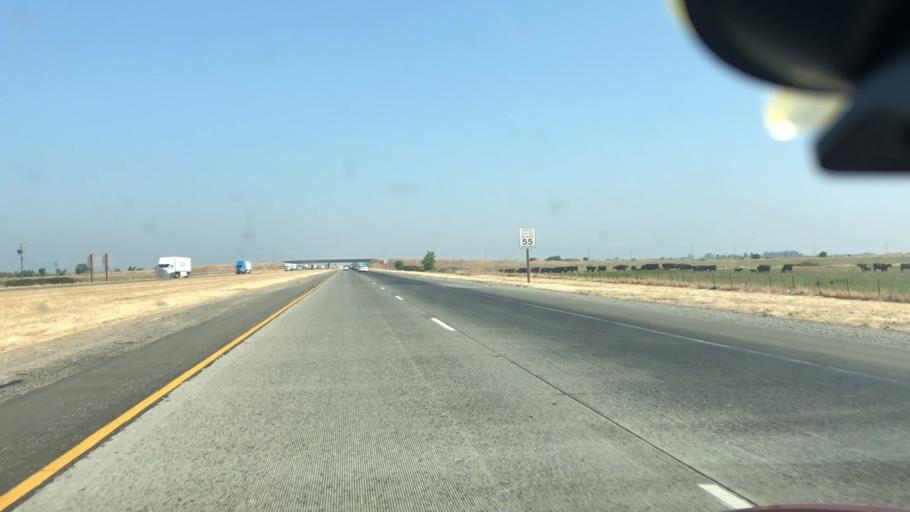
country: US
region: California
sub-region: Sacramento County
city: Walnut Grove
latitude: 38.2924
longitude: -121.4594
